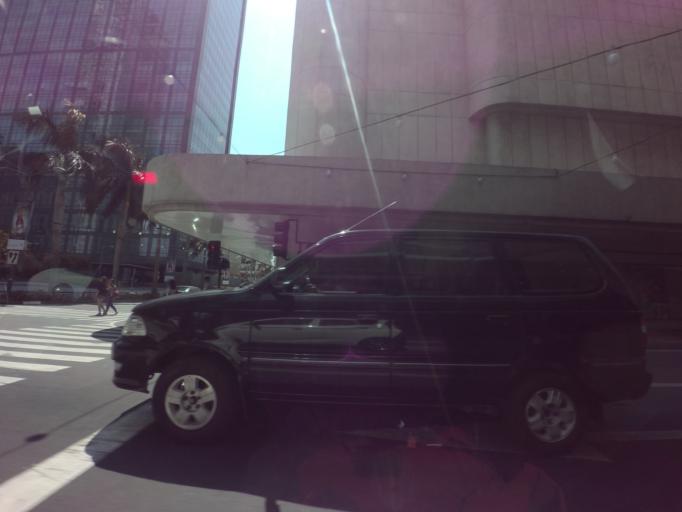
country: PH
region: Metro Manila
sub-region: Makati City
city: Makati City
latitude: 14.5514
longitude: 121.0239
